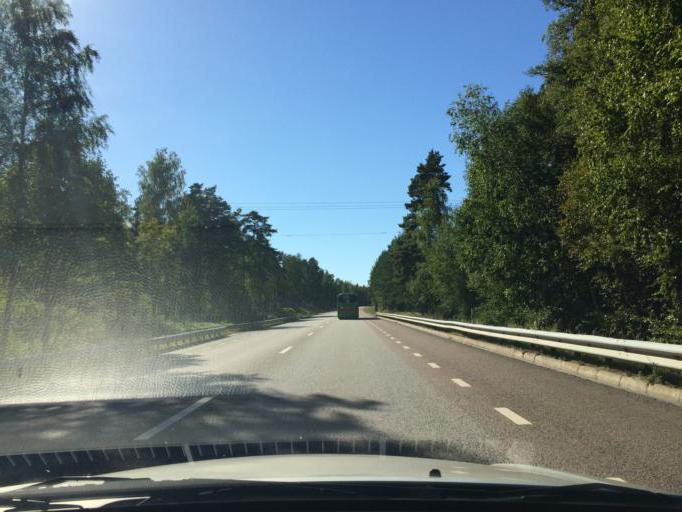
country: SE
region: Soedermanland
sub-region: Eskilstuna Kommun
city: Skogstorp
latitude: 59.3289
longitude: 16.4403
